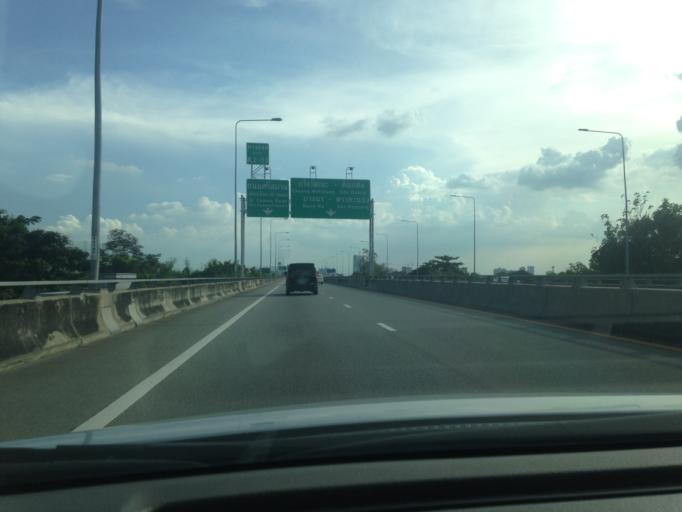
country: TH
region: Bangkok
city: Don Mueang
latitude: 13.9485
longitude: 100.5634
